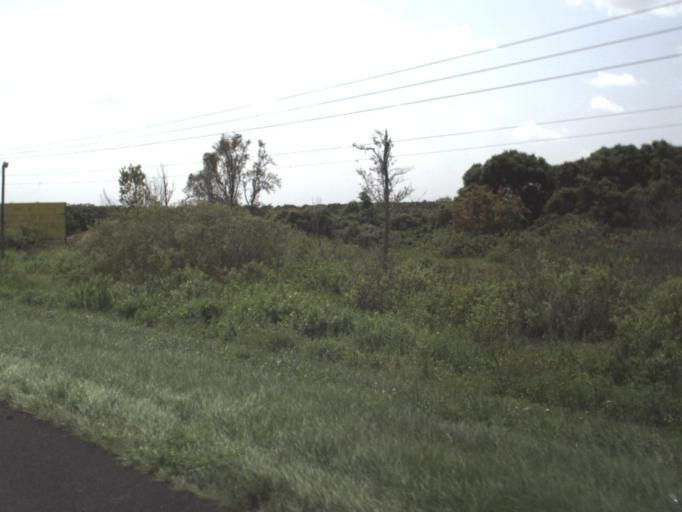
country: US
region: Florida
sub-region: Polk County
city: Frostproof
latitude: 27.6830
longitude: -81.5575
